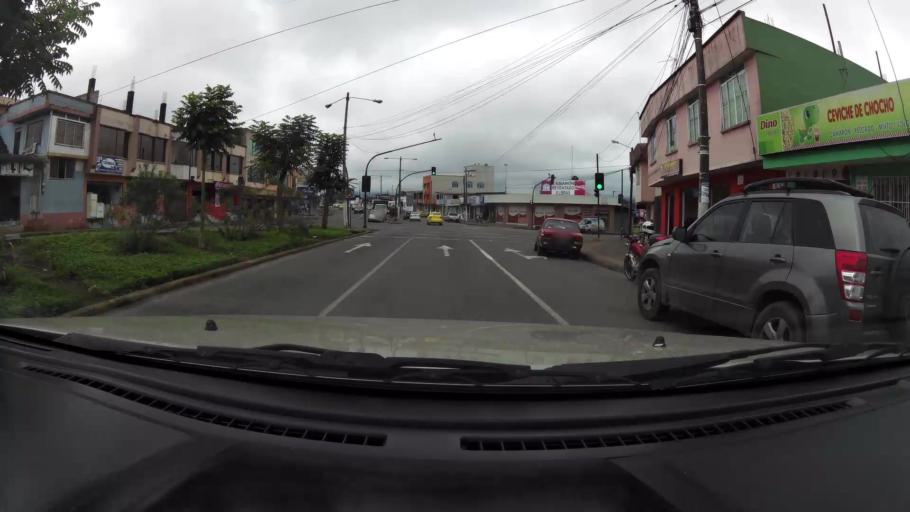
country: EC
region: Santo Domingo de los Tsachilas
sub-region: Canton Santo Domingo de los Colorados
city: Santo Domingo de los Colorados
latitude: -0.2633
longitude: -79.1642
